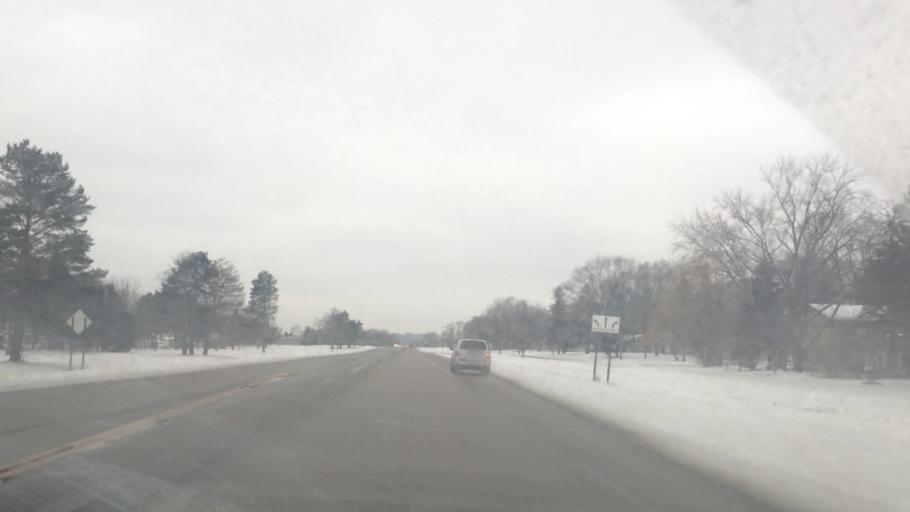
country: US
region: Minnesota
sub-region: Anoka County
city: Lexington
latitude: 45.1345
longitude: -93.1750
